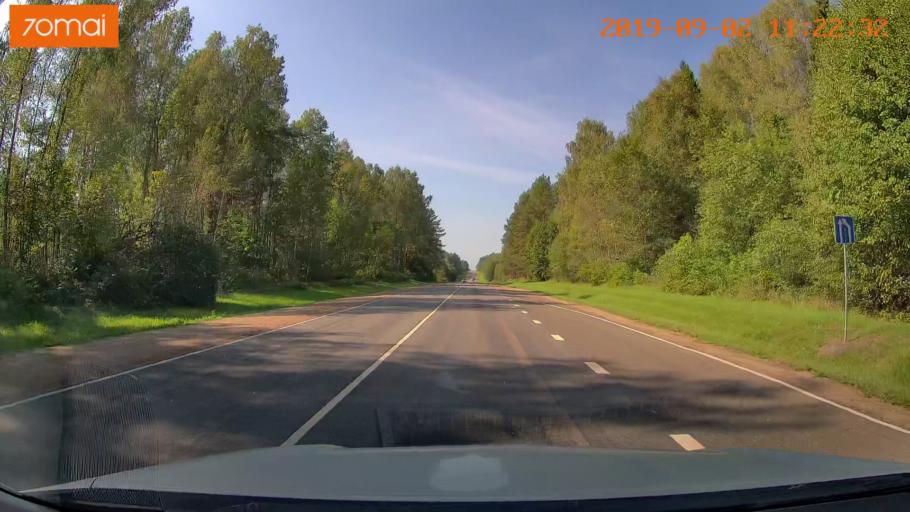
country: RU
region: Smolensk
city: Roslavl'
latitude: 54.0250
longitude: 33.0112
